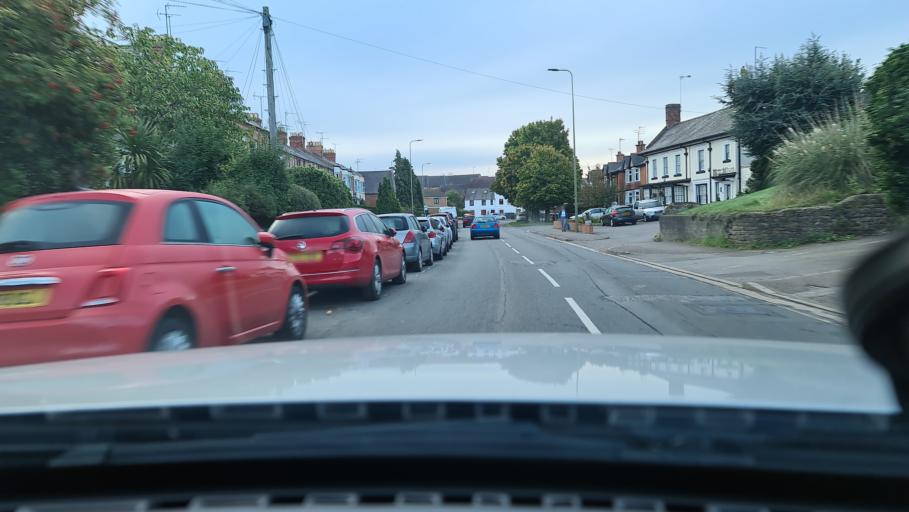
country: GB
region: England
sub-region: Oxfordshire
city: Banbury
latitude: 52.0654
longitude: -1.3476
